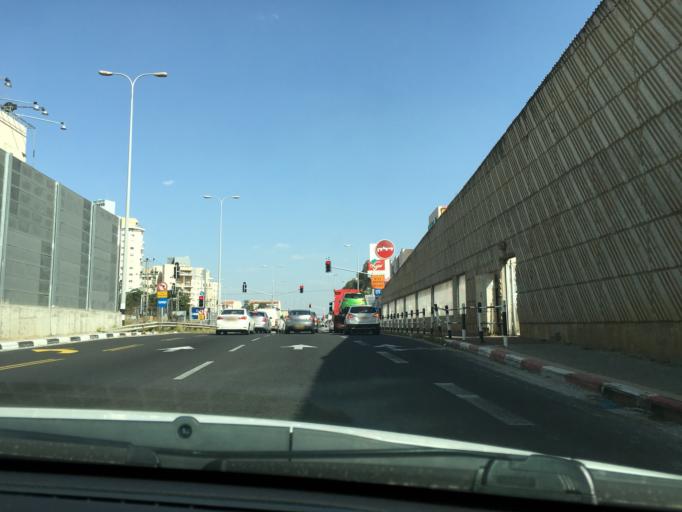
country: IL
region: Central District
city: Hod HaSharon
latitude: 32.1740
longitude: 34.8900
